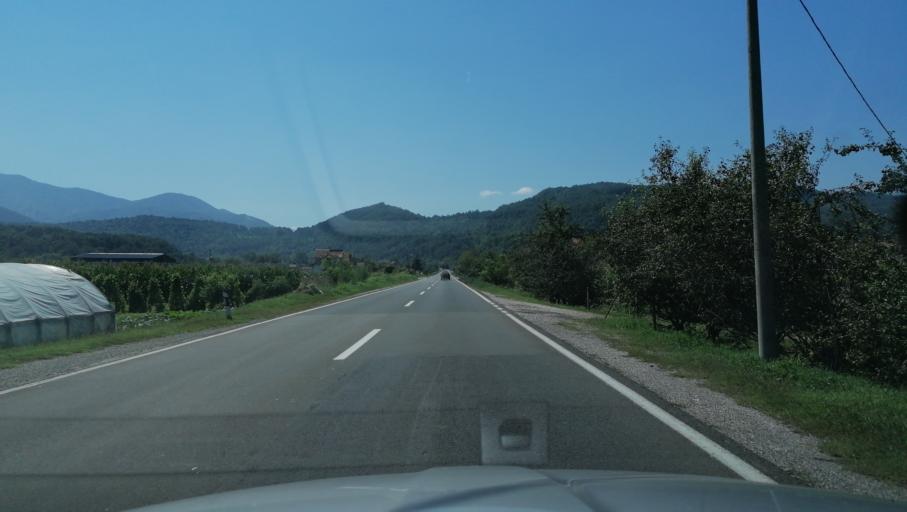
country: RS
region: Central Serbia
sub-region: Raski Okrug
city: Kraljevo
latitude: 43.6883
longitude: 20.5781
